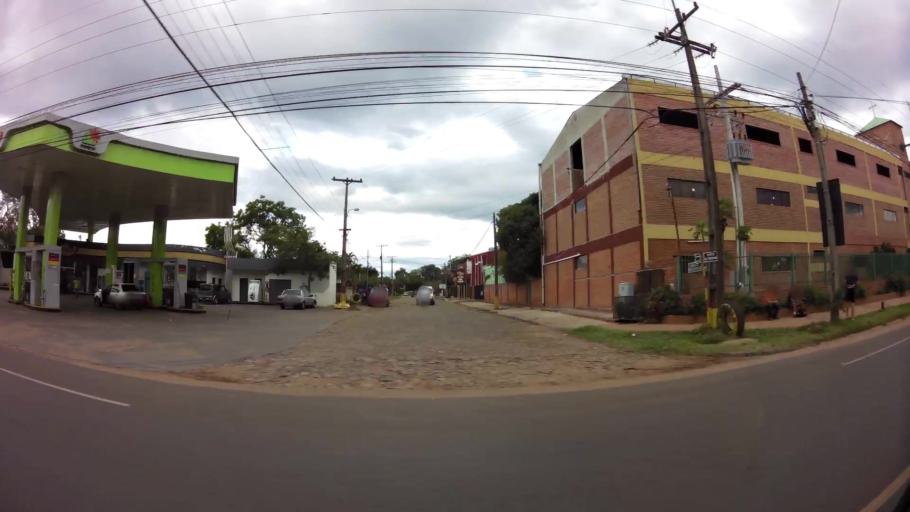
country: PY
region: Central
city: San Lorenzo
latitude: -25.2867
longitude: -57.4999
